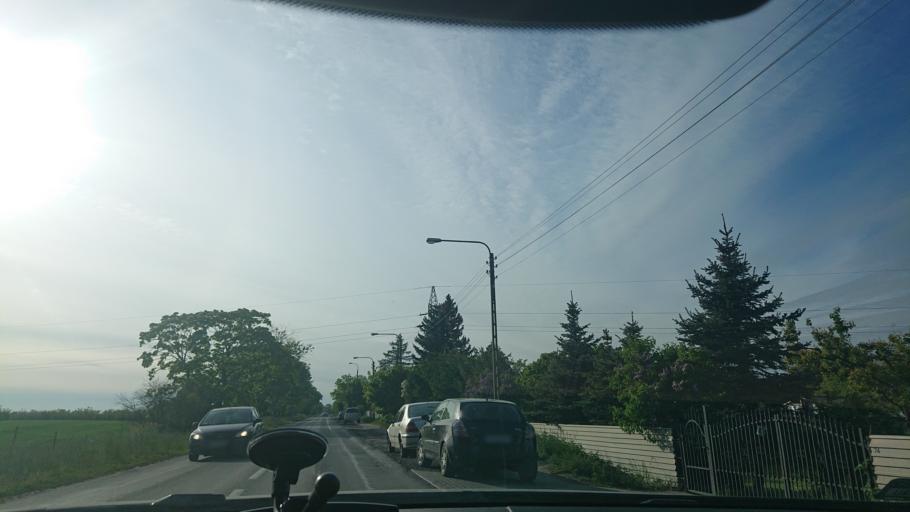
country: PL
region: Greater Poland Voivodeship
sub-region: Powiat gnieznienski
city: Gniezno
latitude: 52.5445
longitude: 17.5672
